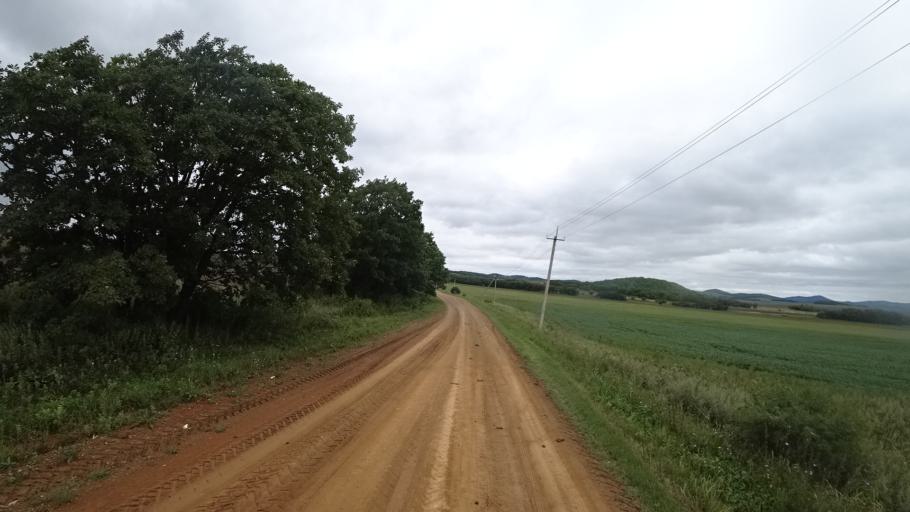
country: RU
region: Primorskiy
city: Chernigovka
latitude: 44.4406
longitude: 132.5942
